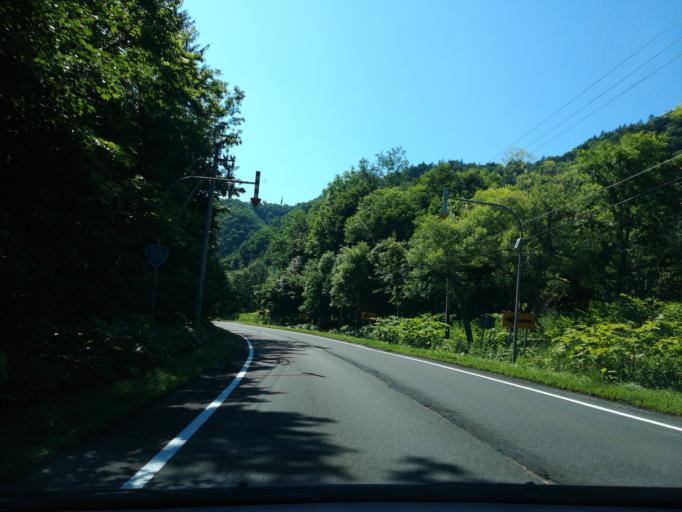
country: JP
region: Hokkaido
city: Chitose
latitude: 42.9168
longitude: 141.9559
